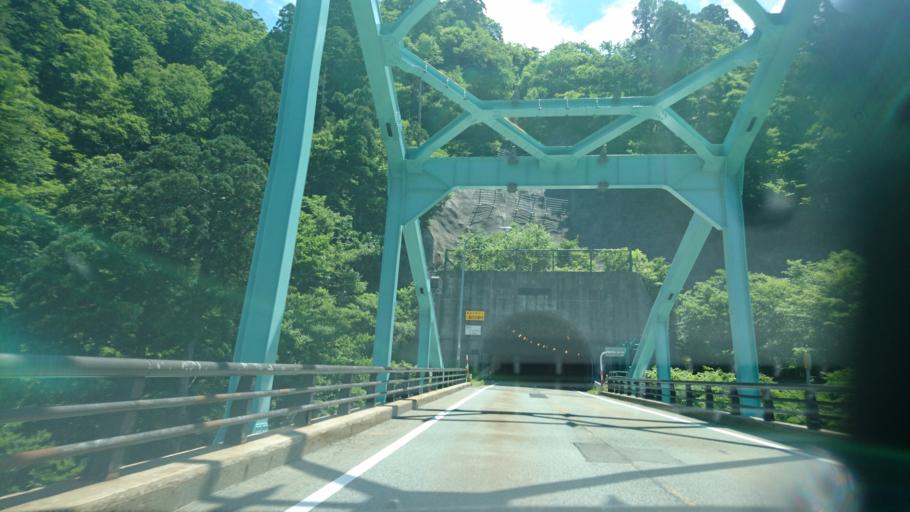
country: JP
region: Iwate
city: Shizukuishi
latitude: 39.6964
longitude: 140.7772
